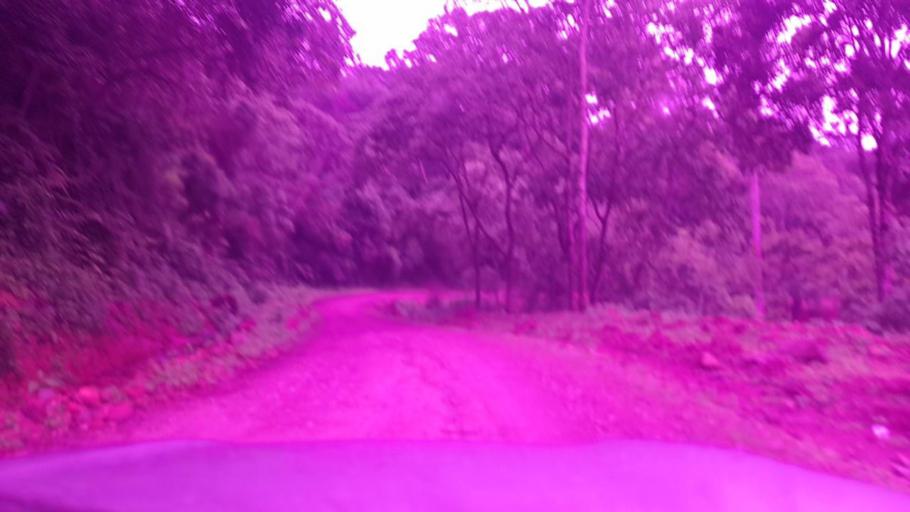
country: ET
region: Southern Nations, Nationalities, and People's Region
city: Bonga
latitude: 7.5121
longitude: 36.0580
